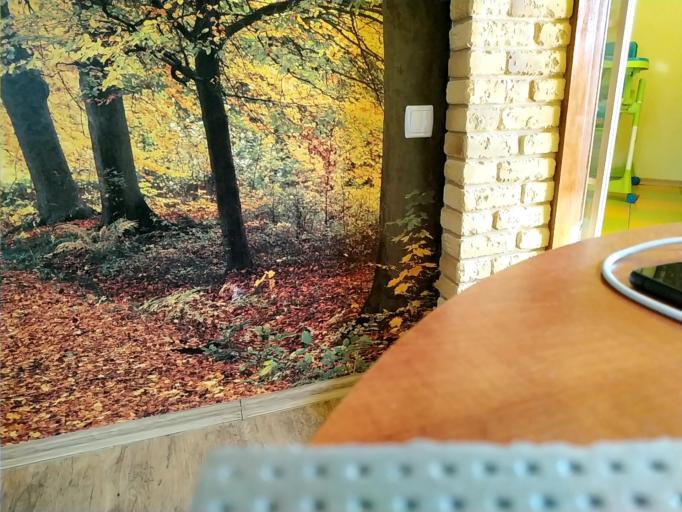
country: RU
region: Tverskaya
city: Kalashnikovo
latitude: 57.3460
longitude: 35.2232
